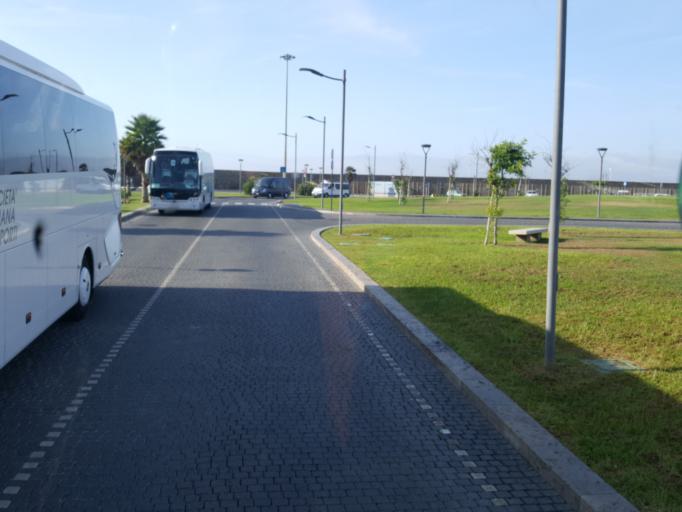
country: IT
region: Latium
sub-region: Citta metropolitana di Roma Capitale
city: Civitavecchia
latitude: 42.0901
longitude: 11.7898
